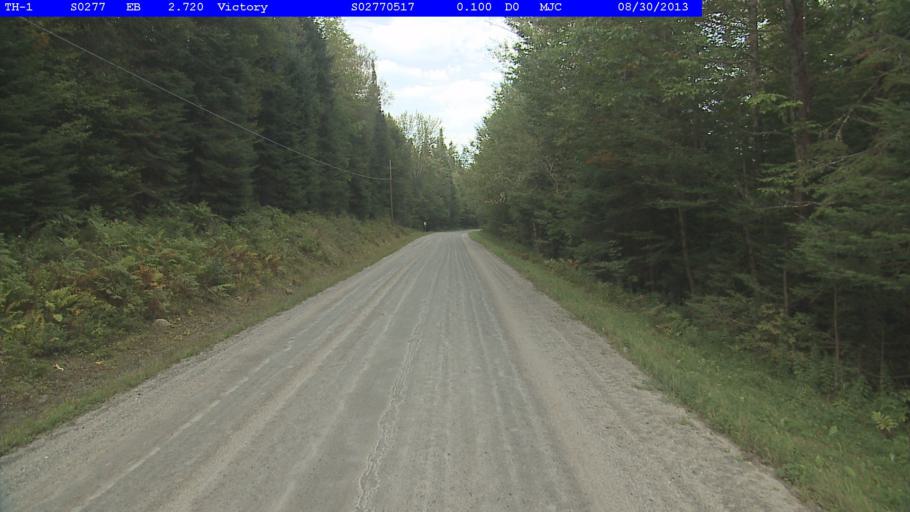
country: US
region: Vermont
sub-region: Caledonia County
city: Lyndonville
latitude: 44.4976
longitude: -71.8543
